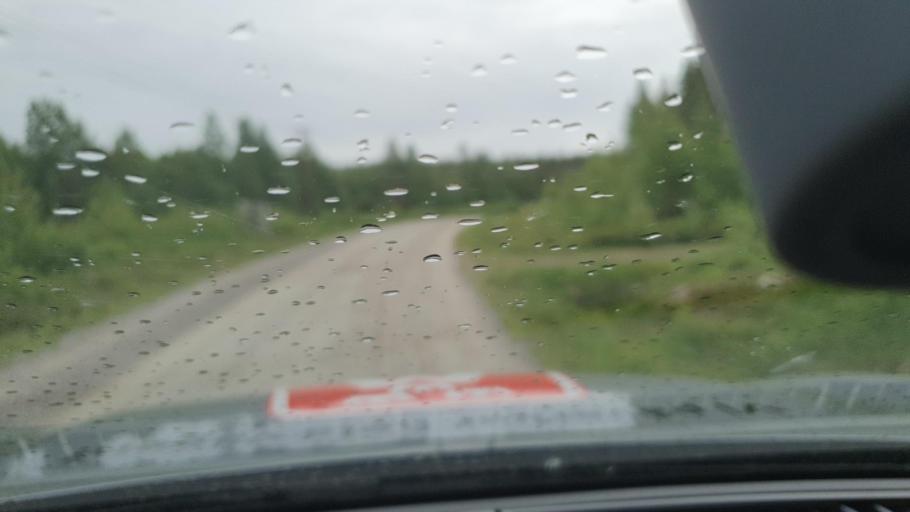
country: SE
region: Norrbotten
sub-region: Kalix Kommun
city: Kalix
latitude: 66.0134
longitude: 23.1316
